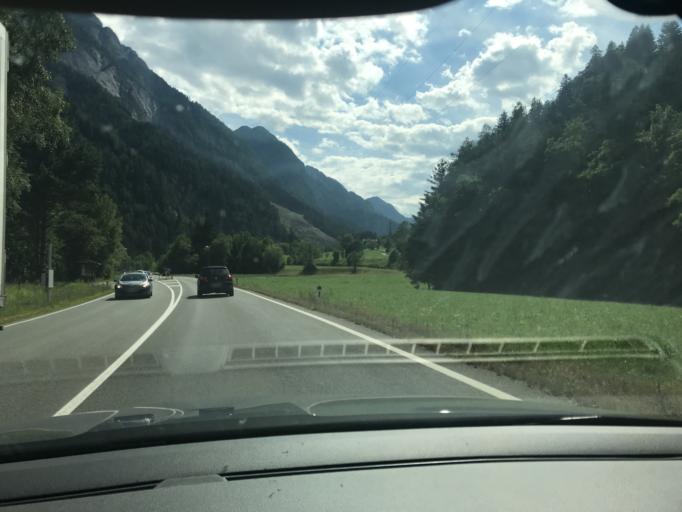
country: AT
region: Tyrol
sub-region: Politischer Bezirk Lienz
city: Leisach
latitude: 46.7982
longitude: 12.7360
